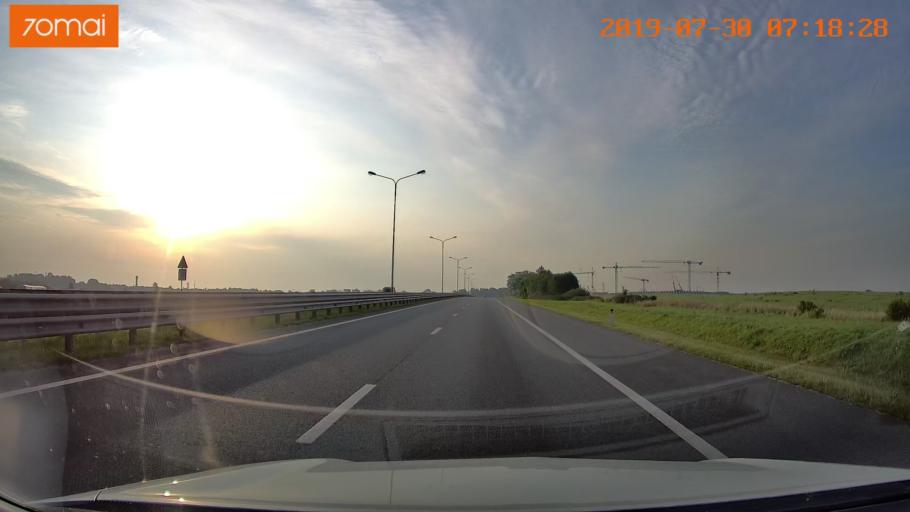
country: RU
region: Kaliningrad
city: Bol'shoe Isakovo
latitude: 54.7040
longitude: 20.6487
